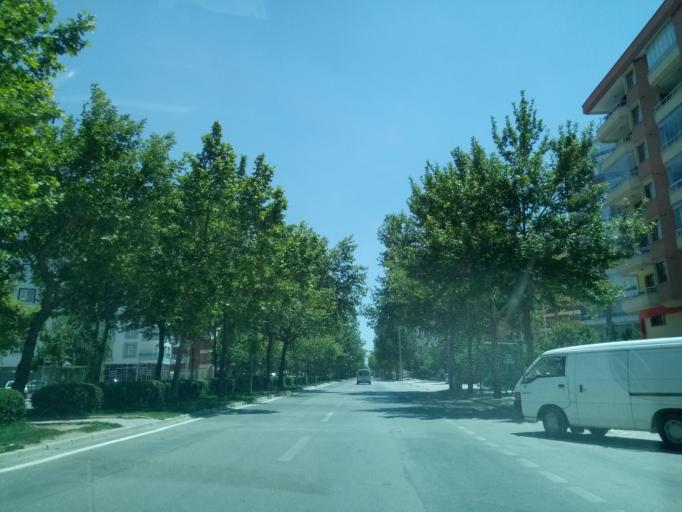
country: TR
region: Konya
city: Konya
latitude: 37.8486
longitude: 32.5034
